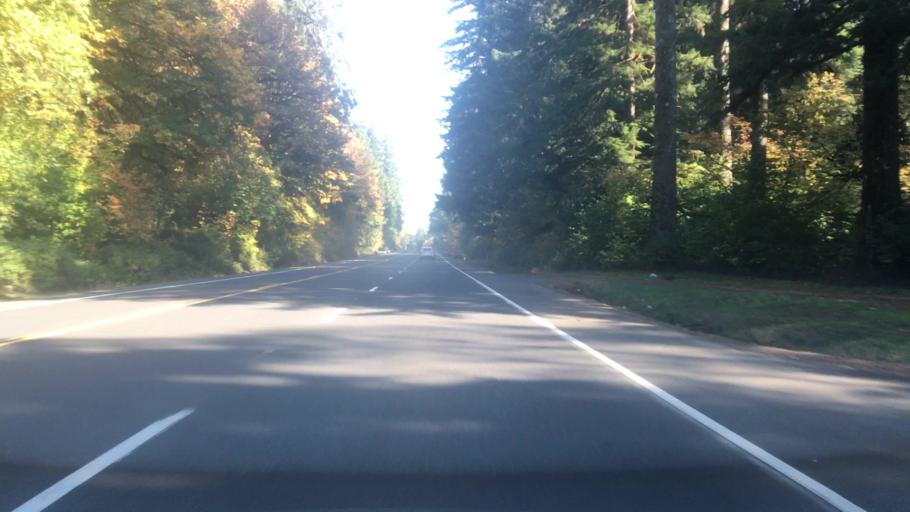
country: US
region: Oregon
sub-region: Lincoln County
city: Rose Lodge
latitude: 45.0478
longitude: -123.7941
